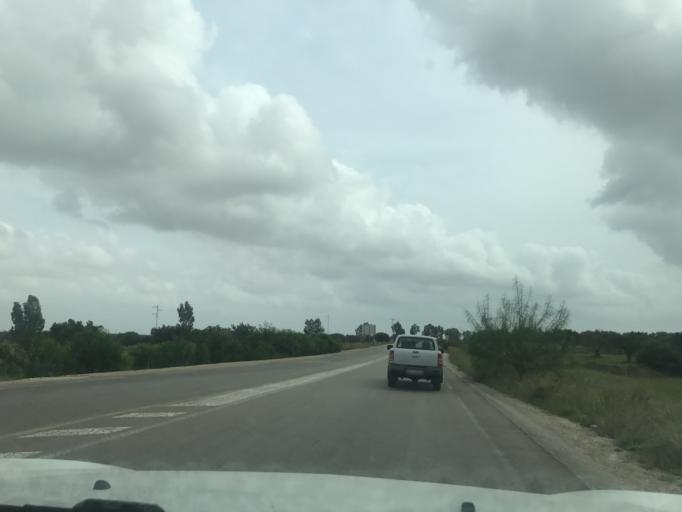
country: TN
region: Al Munastir
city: Sidi Bin Nur
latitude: 35.5442
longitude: 10.8778
